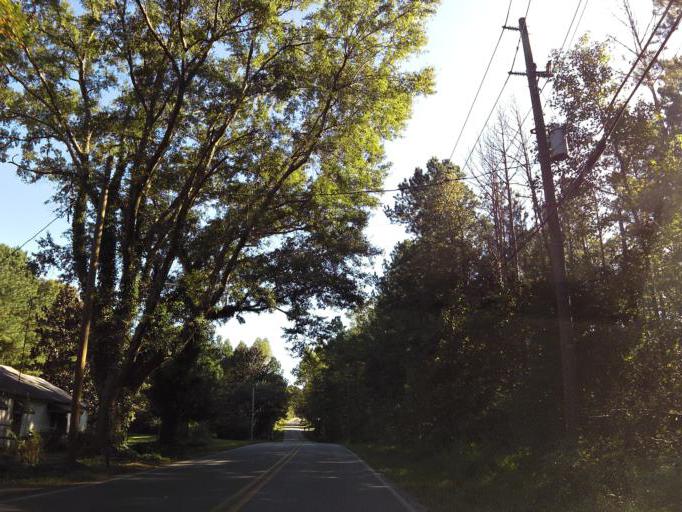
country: US
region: Georgia
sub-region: Cobb County
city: Acworth
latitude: 34.1241
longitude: -84.6801
